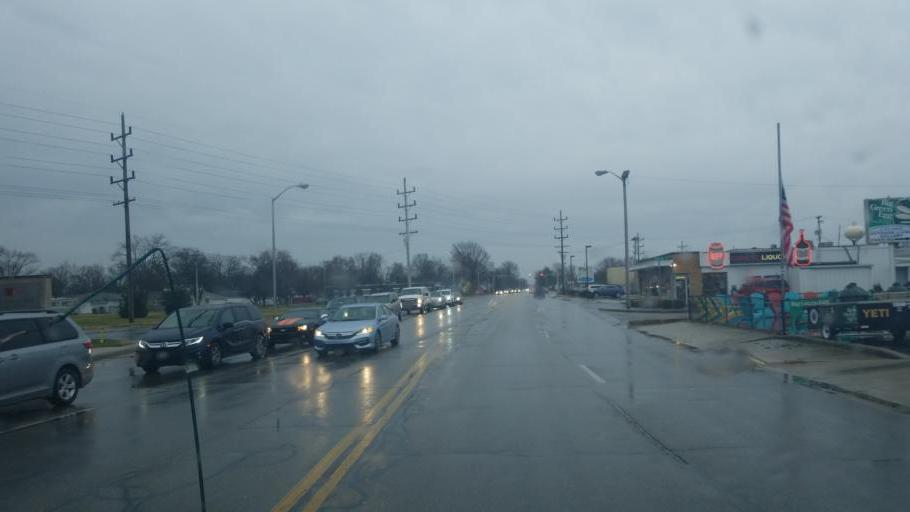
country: US
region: Indiana
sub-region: Bartholomew County
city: Columbus
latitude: 39.2226
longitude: -85.9042
